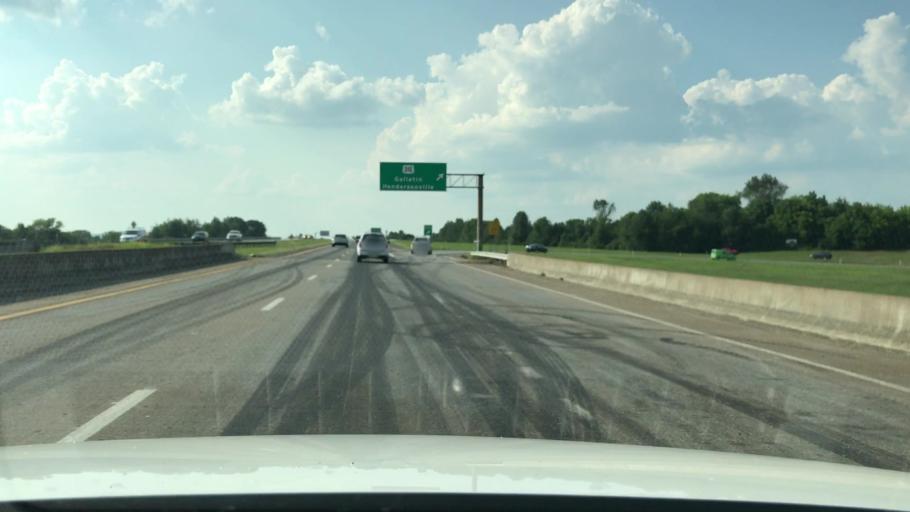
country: US
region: Tennessee
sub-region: Sumner County
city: Gallatin
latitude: 36.3785
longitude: -86.4678
